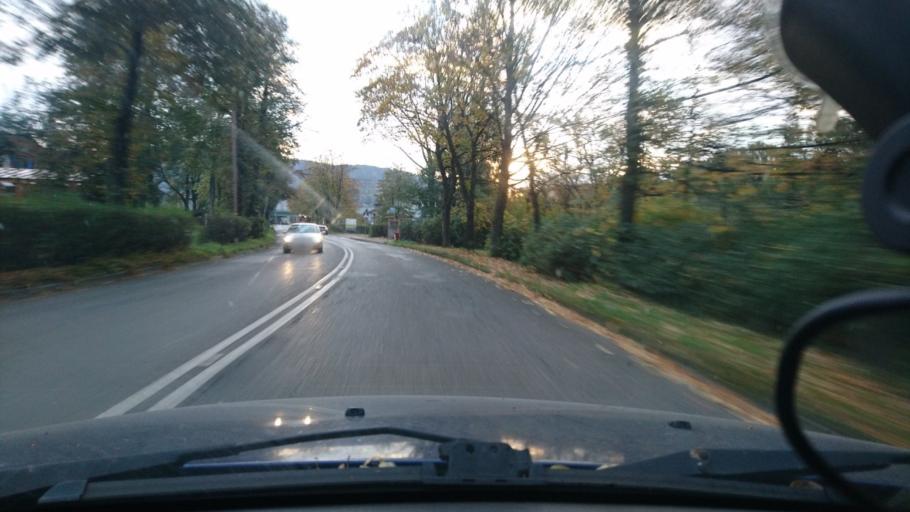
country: PL
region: Silesian Voivodeship
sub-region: Bielsko-Biala
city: Bielsko-Biala
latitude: 49.8019
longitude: 19.0767
